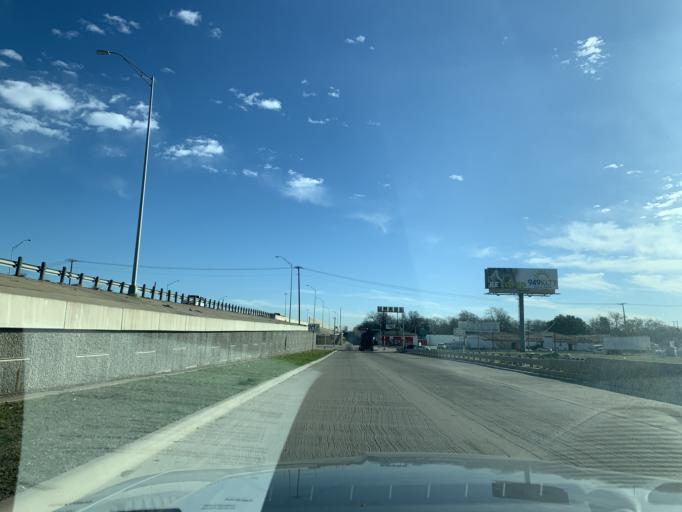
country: US
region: Texas
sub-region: Dallas County
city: Grand Prairie
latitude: 32.7617
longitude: -96.9618
